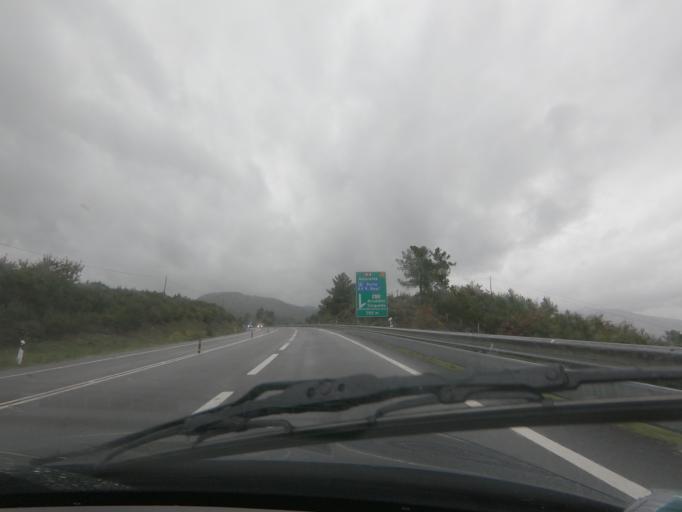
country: PT
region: Vila Real
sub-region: Vila Real
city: Vila Real
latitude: 41.2790
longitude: -7.7973
